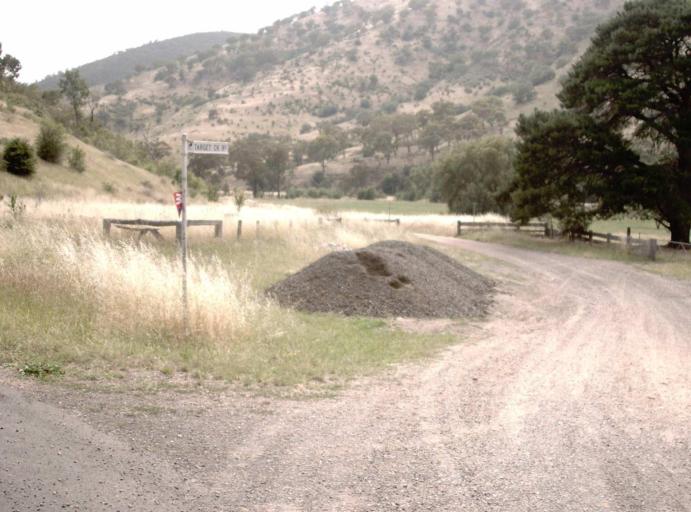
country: AU
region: Victoria
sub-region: Wellington
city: Heyfield
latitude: -37.6266
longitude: 146.6240
